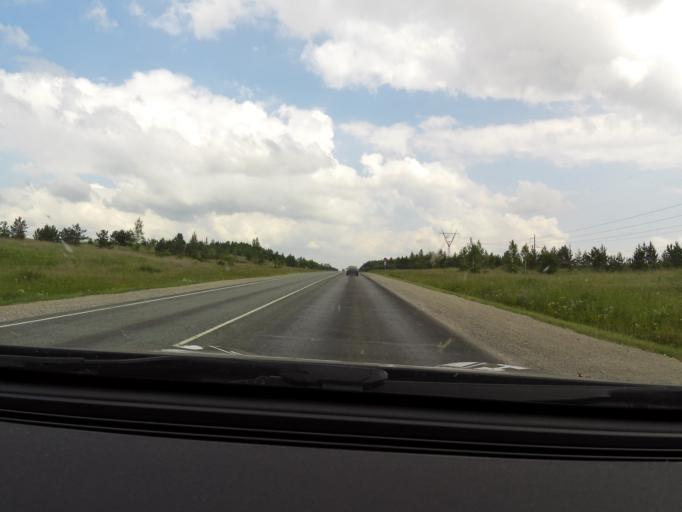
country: RU
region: Sverdlovsk
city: Achit
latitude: 56.7820
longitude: 57.9140
